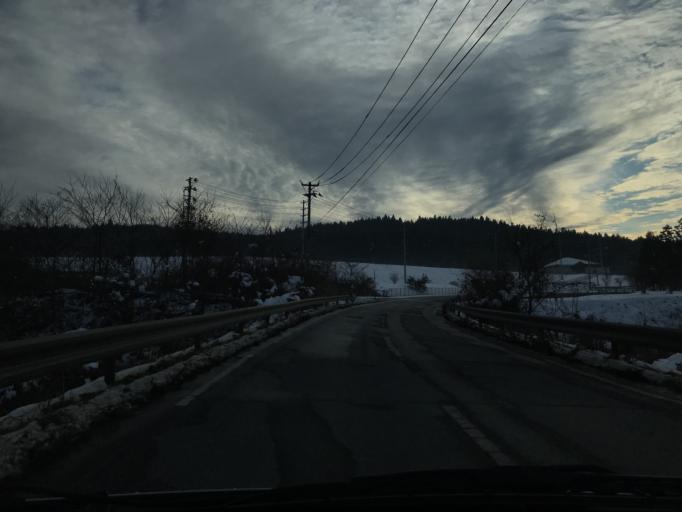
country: JP
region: Iwate
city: Mizusawa
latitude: 39.0529
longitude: 141.0814
